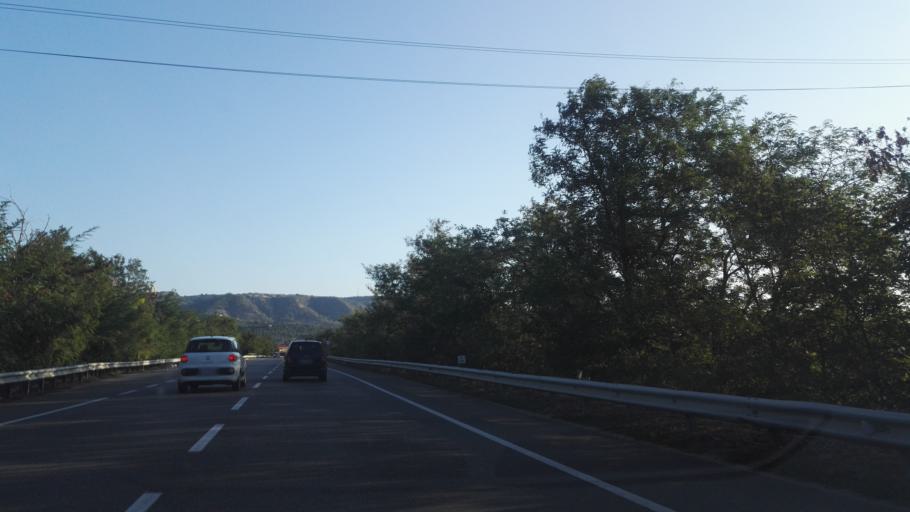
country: IT
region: Calabria
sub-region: Provincia di Catanzaro
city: Montepaone Lido
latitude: 38.7164
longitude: 16.5326
